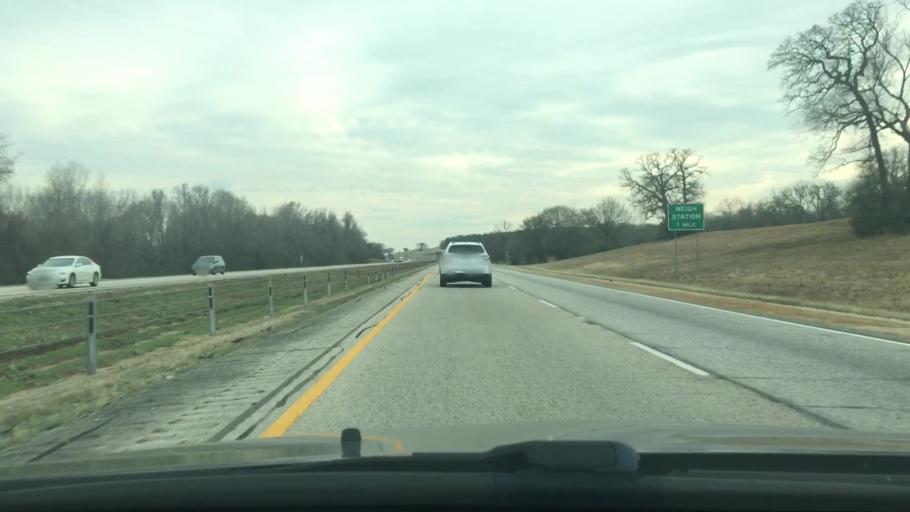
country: US
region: Texas
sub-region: Leon County
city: Centerville
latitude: 31.2998
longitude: -95.9997
